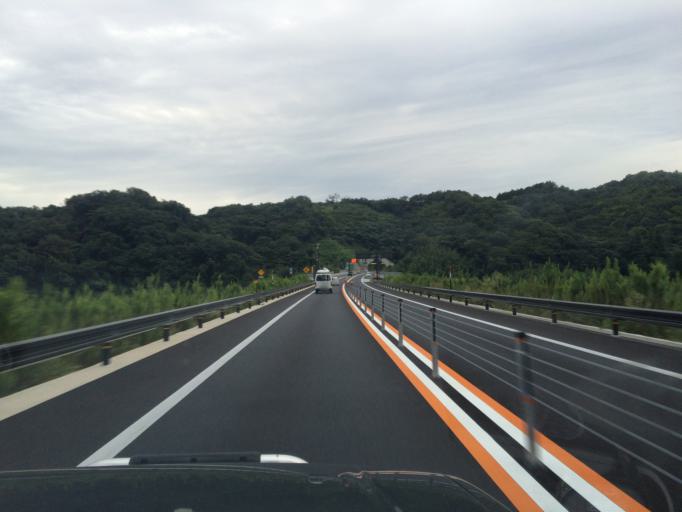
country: JP
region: Tottori
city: Tottori
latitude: 35.4933
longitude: 134.1912
